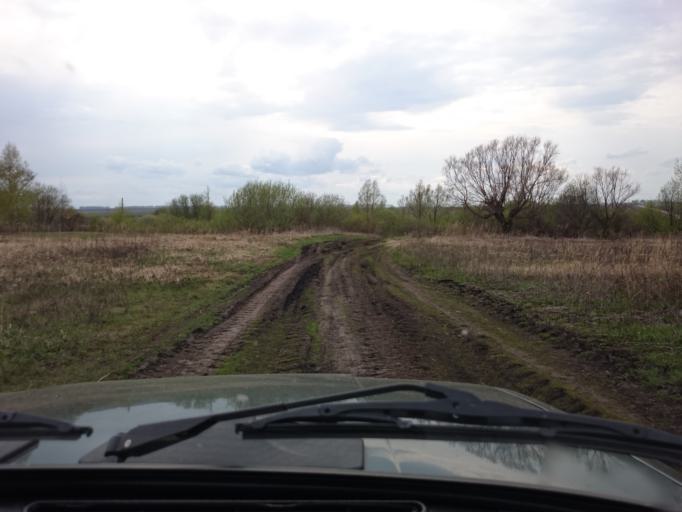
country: RU
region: Mordoviya
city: Kadoshkino
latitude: 54.0177
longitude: 44.4595
